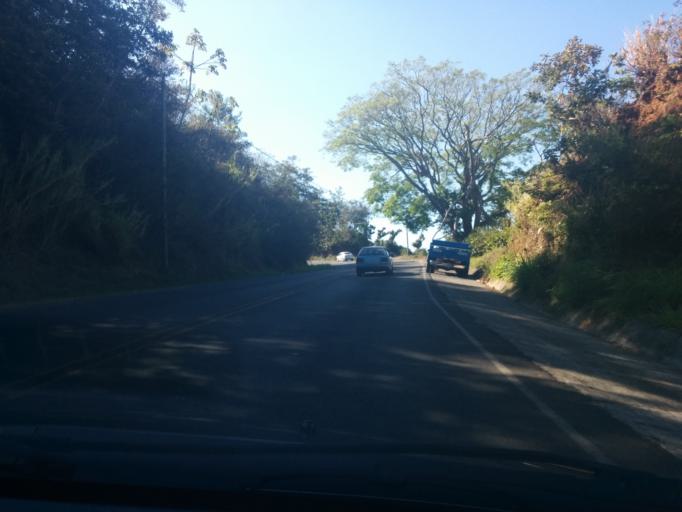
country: CR
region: Alajuela
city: San Rafael
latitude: 10.0370
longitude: -84.5070
